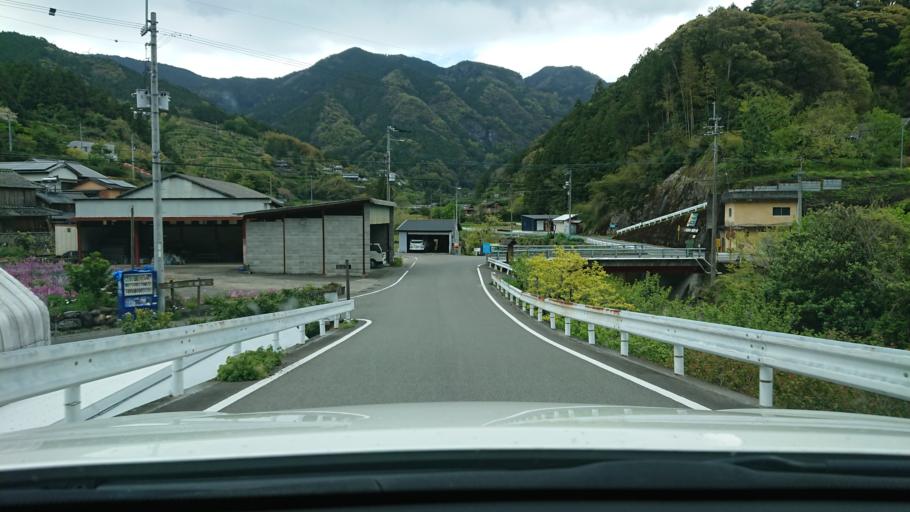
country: JP
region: Tokushima
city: Ishii
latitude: 33.9224
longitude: 134.4233
